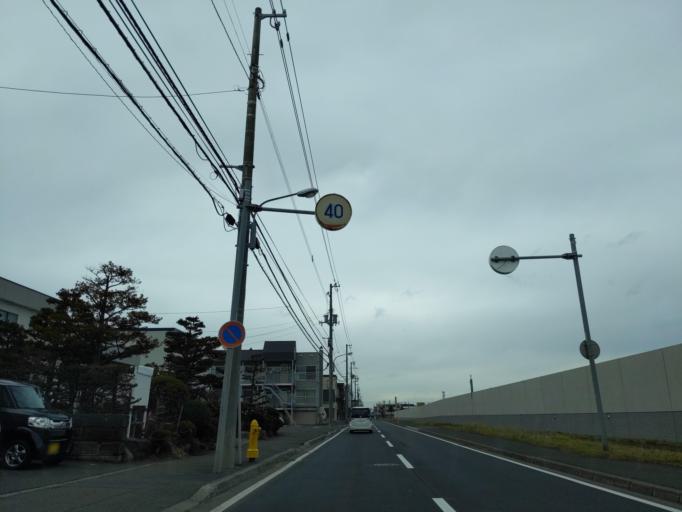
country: JP
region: Hokkaido
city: Sapporo
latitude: 43.0835
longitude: 141.3950
